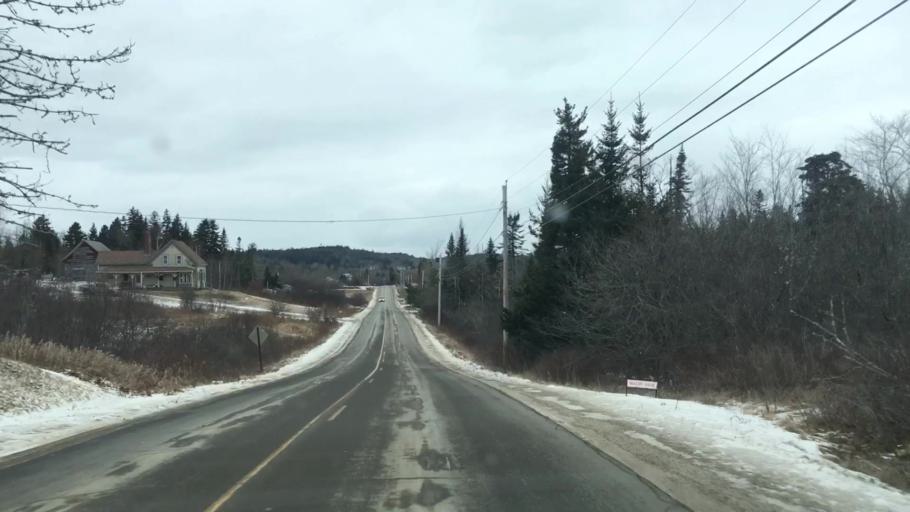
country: US
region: Maine
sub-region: Washington County
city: Machiasport
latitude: 44.7076
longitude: -67.4026
